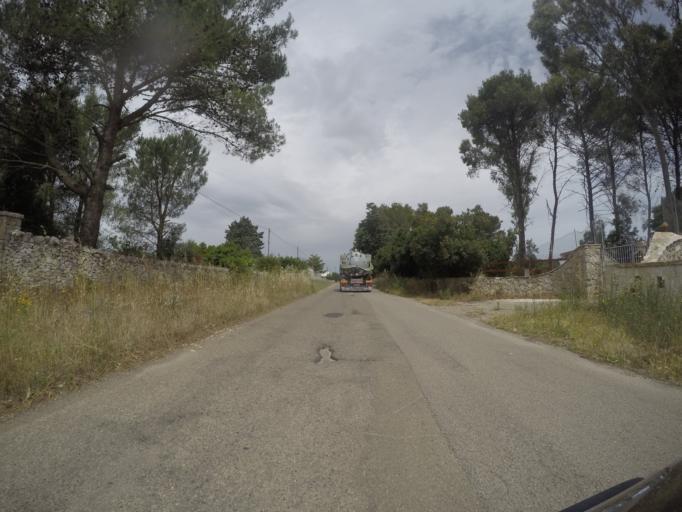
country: IT
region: Apulia
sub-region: Provincia di Taranto
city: Martina Franca
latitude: 40.6642
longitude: 17.3482
